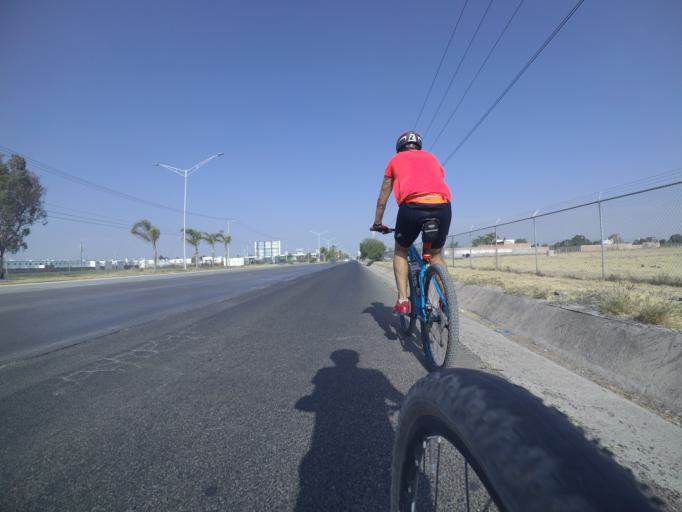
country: MX
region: Aguascalientes
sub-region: Jesus Maria
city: Arboledas Paso Blanco [Fraccionamiento]
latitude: 21.9463
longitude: -102.2989
